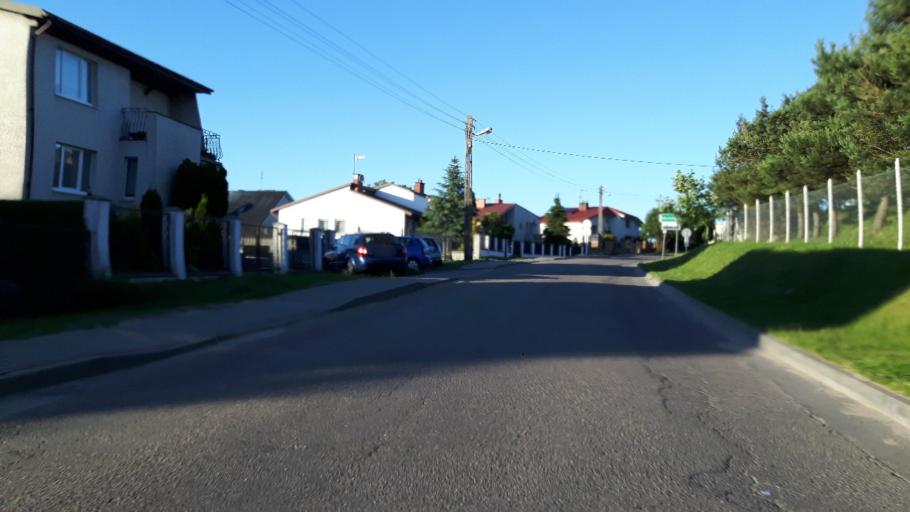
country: PL
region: Pomeranian Voivodeship
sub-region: Powiat pucki
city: Mosty
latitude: 54.6105
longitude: 18.5030
